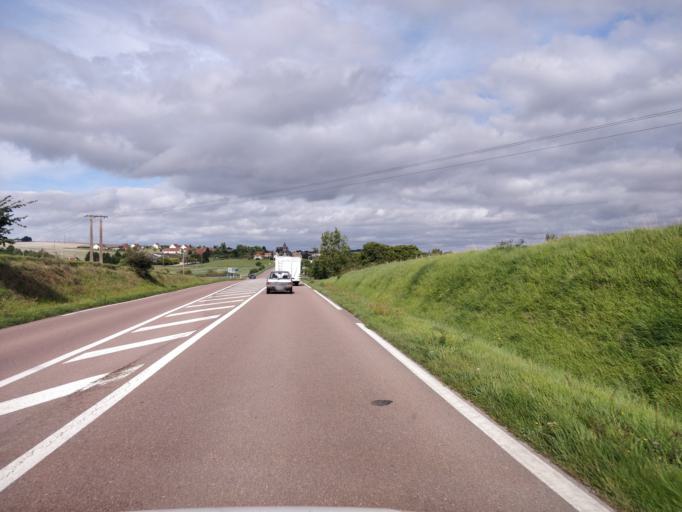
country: FR
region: Champagne-Ardenne
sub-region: Departement de l'Aube
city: Aix-en-Othe
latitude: 48.2502
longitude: 3.7175
